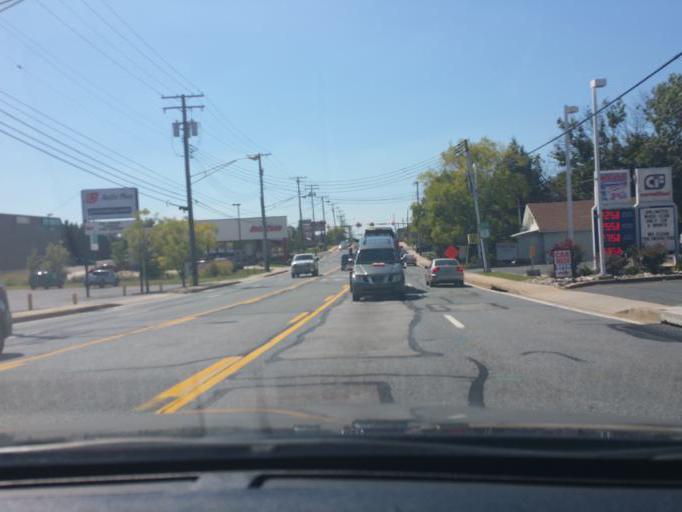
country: US
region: Maryland
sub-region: Harford County
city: Bel Air
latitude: 39.5308
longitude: -76.3503
